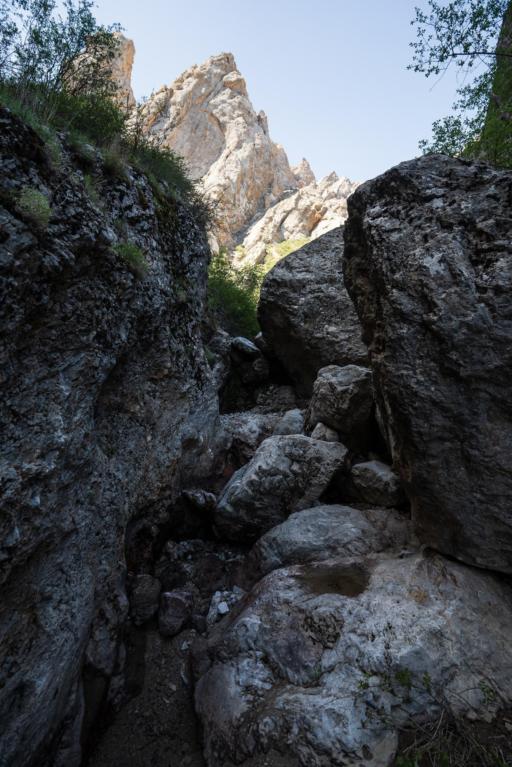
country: KZ
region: Ongtustik Qazaqstan
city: Ashchysay
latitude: 43.7706
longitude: 68.7958
